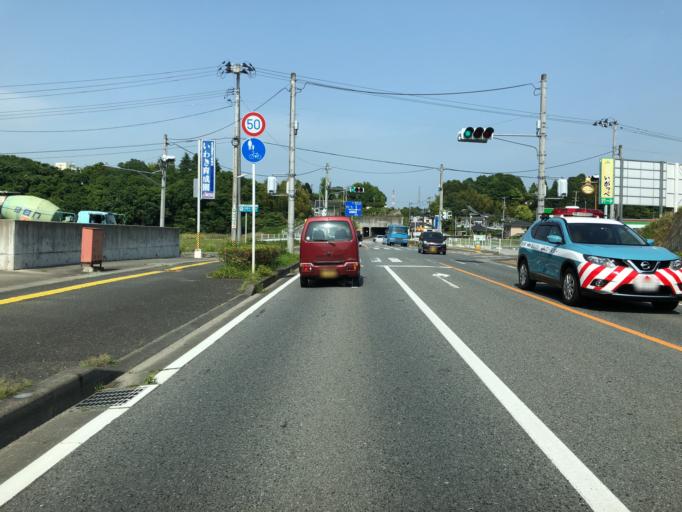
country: JP
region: Ibaraki
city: Kitaibaraki
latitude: 36.9232
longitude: 140.7875
